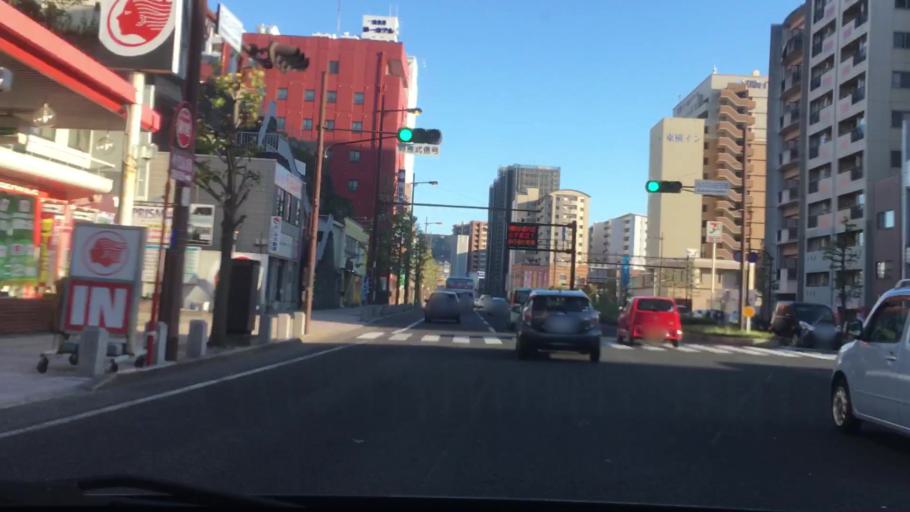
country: JP
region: Nagasaki
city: Sasebo
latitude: 33.1661
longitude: 129.7253
